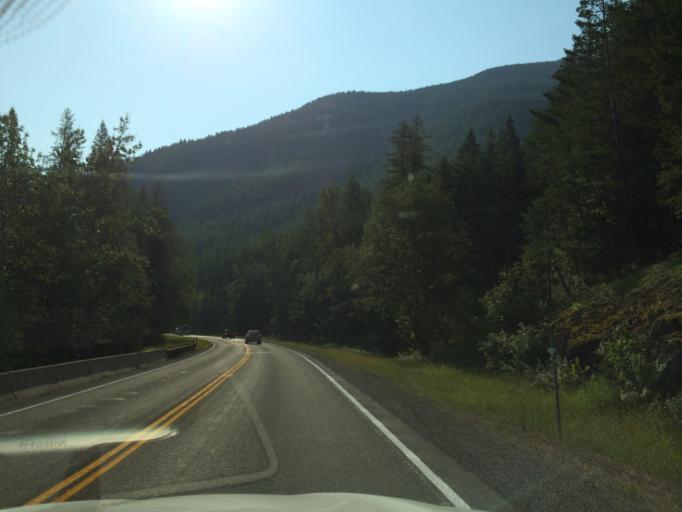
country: US
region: Montana
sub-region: Flathead County
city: Columbia Falls
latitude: 48.4926
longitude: -113.9108
